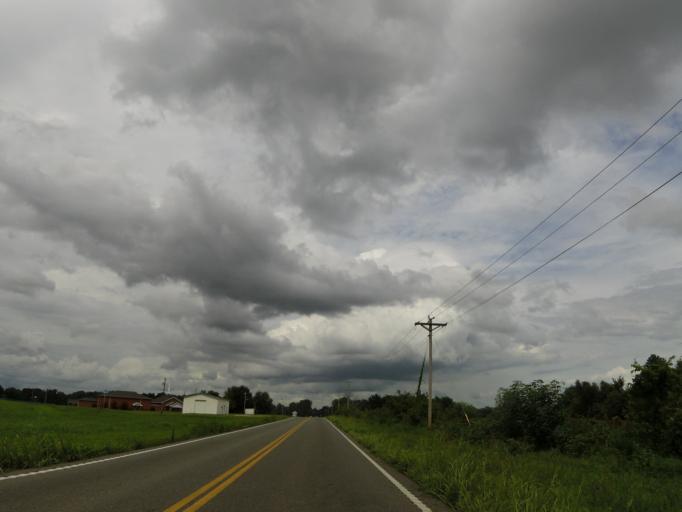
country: US
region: Kentucky
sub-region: Ballard County
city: La Center
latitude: 36.9984
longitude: -88.8773
